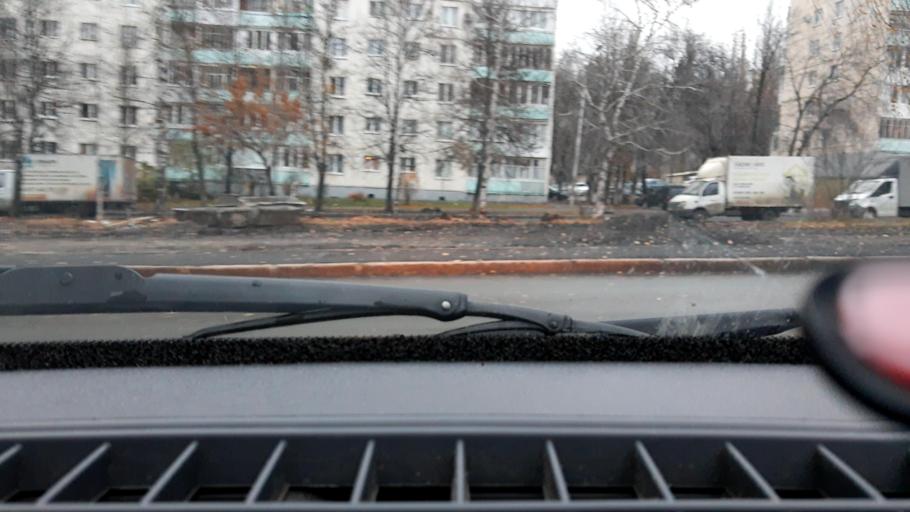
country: RU
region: Bashkortostan
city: Ufa
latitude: 54.7424
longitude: 56.0232
